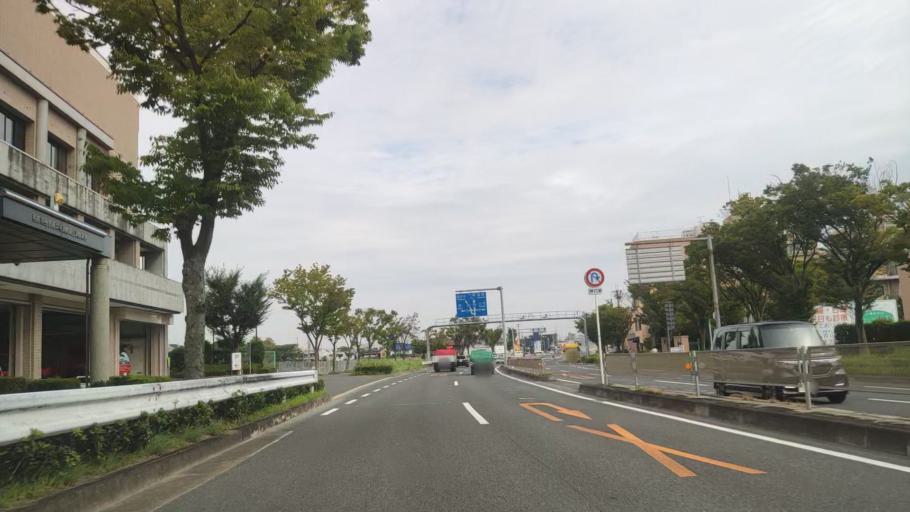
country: JP
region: Osaka
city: Kashihara
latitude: 34.5546
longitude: 135.5985
